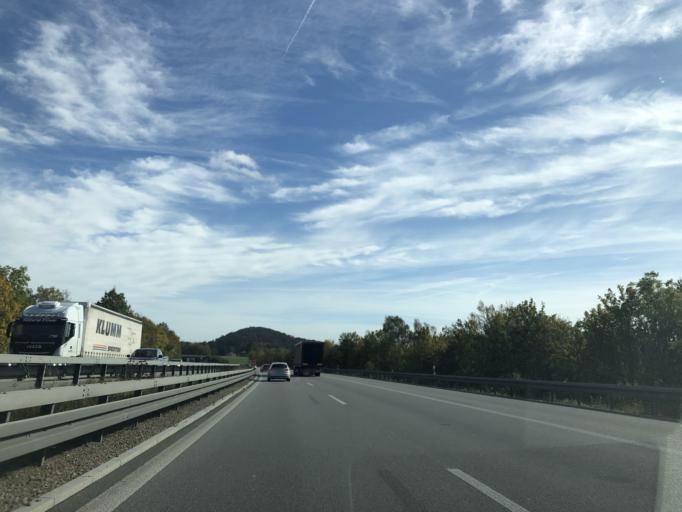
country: DE
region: Bavaria
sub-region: Upper Palatinate
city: Parsberg
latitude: 49.1841
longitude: 11.6898
